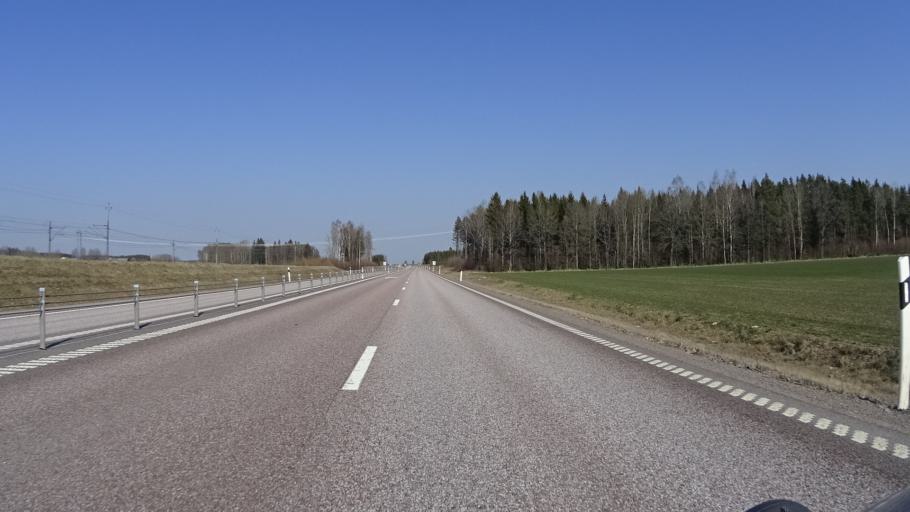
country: SE
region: OEstergoetland
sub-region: Motala Kommun
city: Stenstorp
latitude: 58.4234
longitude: 15.0694
